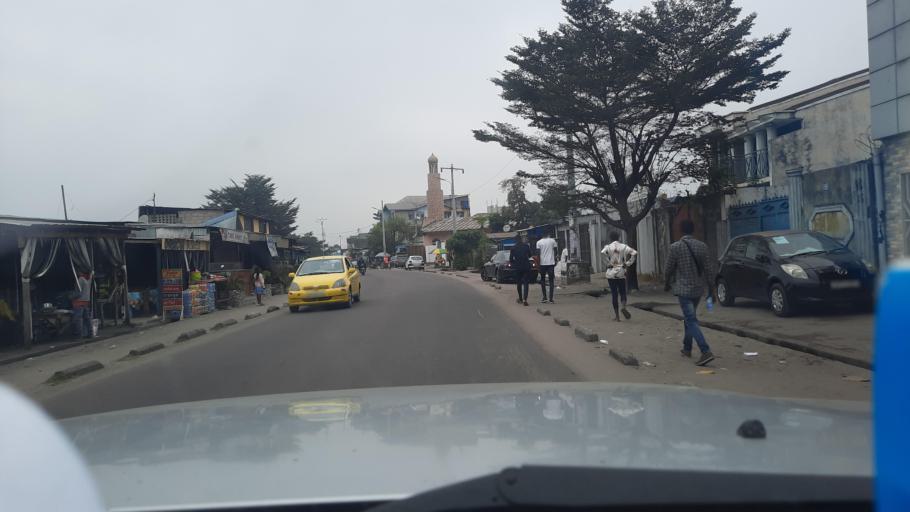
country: CD
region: Kinshasa
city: Masina
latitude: -4.3826
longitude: 15.3444
